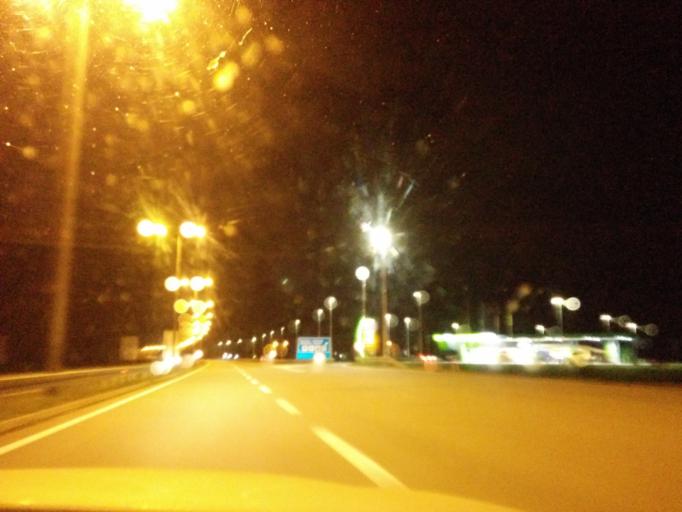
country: RS
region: Autonomna Pokrajina Vojvodina
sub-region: Sremski Okrug
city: Sid
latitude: 45.0485
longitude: 19.1894
